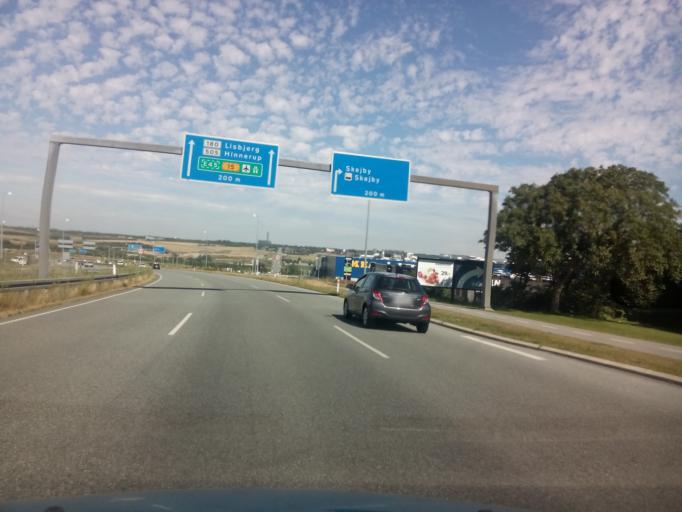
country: DK
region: Central Jutland
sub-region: Arhus Kommune
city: Arhus
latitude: 56.2006
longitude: 10.1813
